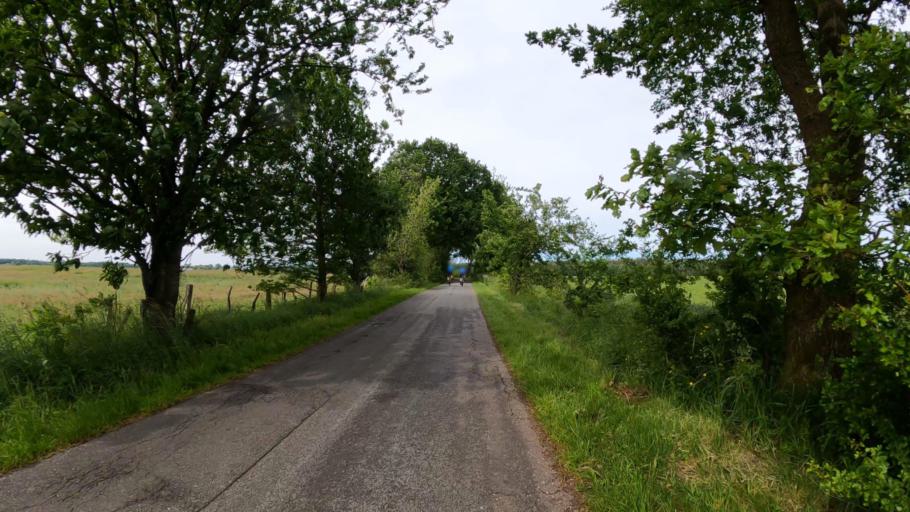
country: DE
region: Schleswig-Holstein
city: Hartenholm
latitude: 53.8869
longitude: 10.0811
